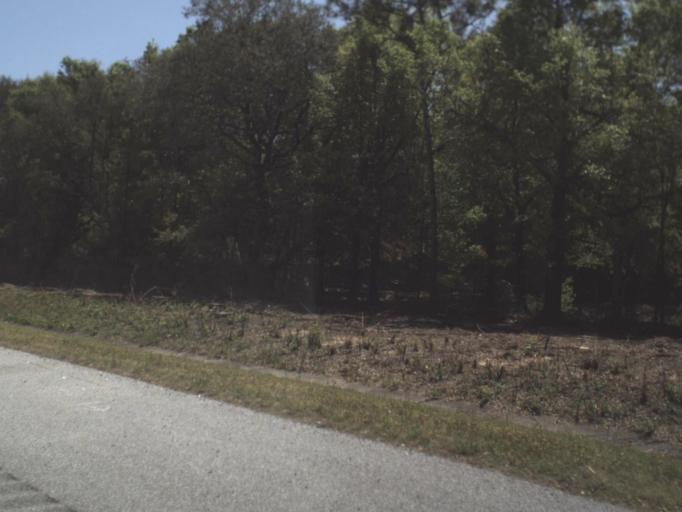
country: US
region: Florida
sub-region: Escambia County
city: Ferry Pass
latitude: 30.5020
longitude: -87.1724
